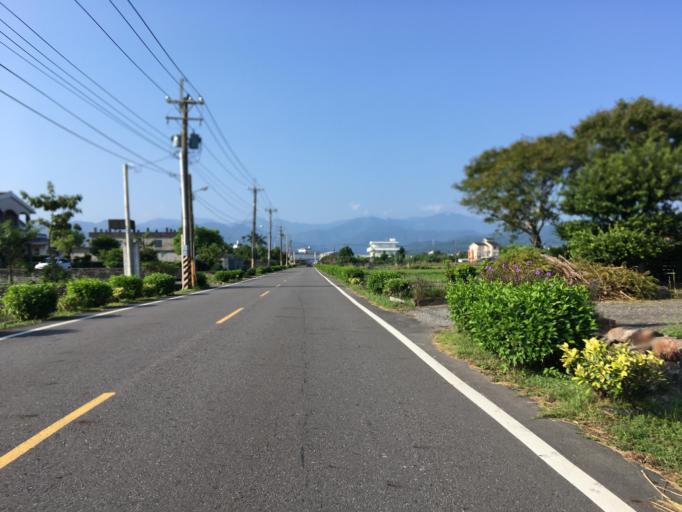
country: TW
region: Taiwan
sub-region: Yilan
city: Yilan
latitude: 24.6772
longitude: 121.7339
